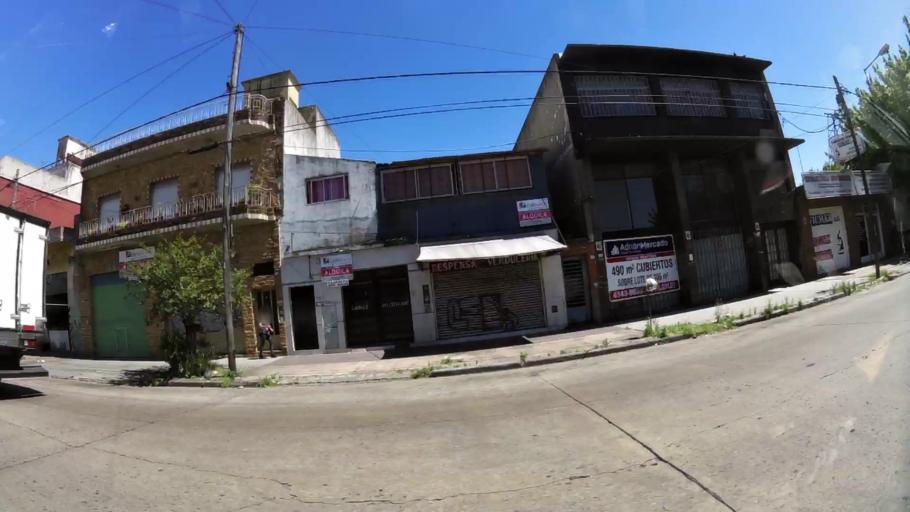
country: AR
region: Buenos Aires
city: Caseros
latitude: -34.5856
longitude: -58.5594
